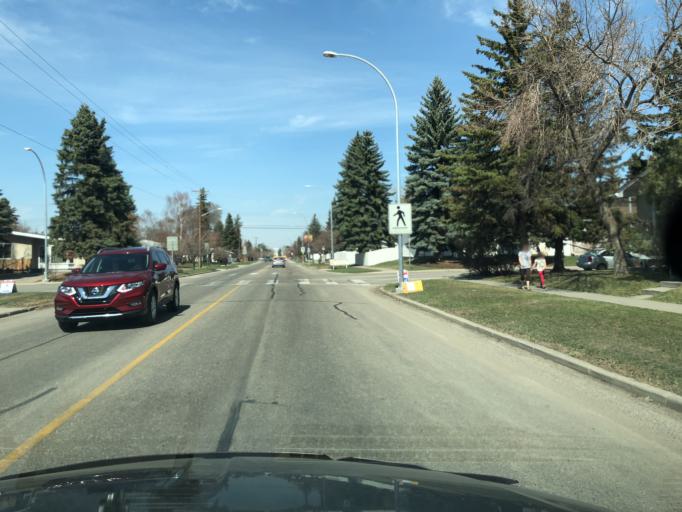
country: CA
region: Alberta
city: Calgary
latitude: 50.9656
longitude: -114.0485
